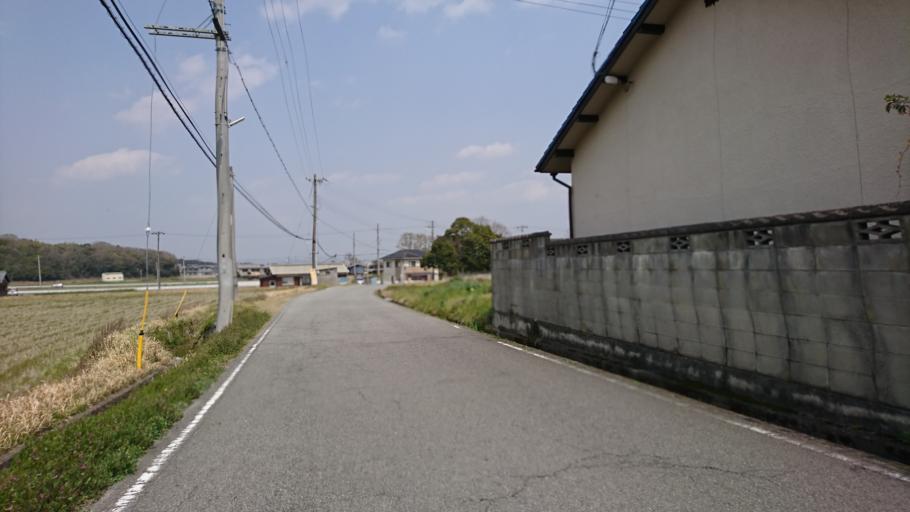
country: JP
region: Hyogo
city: Ono
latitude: 34.8328
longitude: 134.9046
